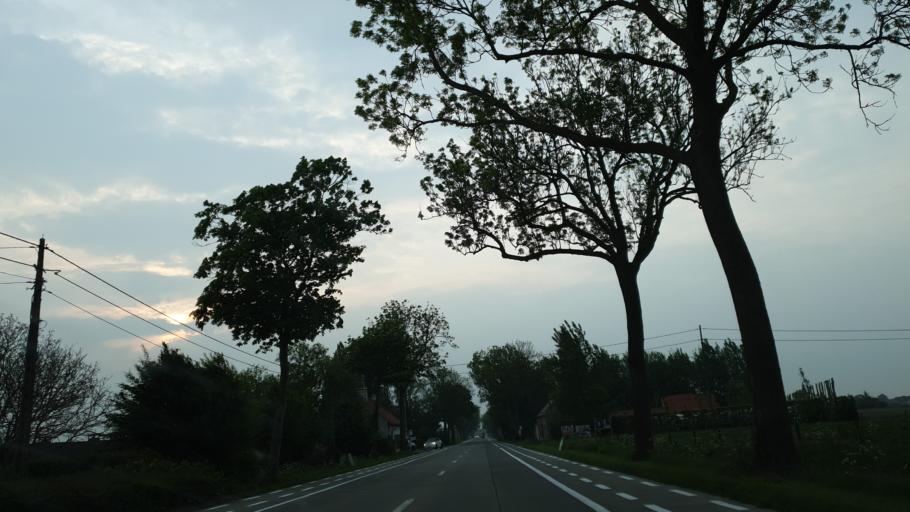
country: BE
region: Flanders
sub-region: Provincie West-Vlaanderen
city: Poperinge
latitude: 50.9254
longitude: 2.7475
